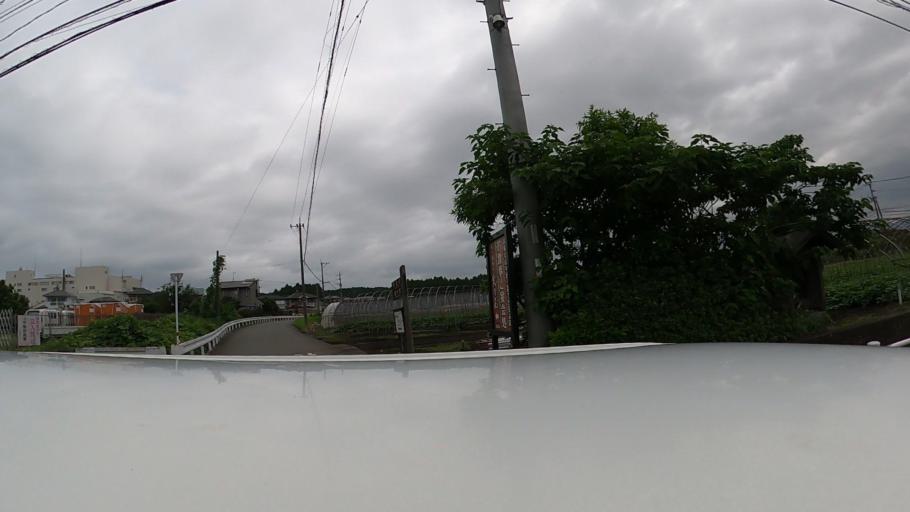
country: JP
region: Kumamoto
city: Ozu
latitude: 32.8382
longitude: 130.8902
